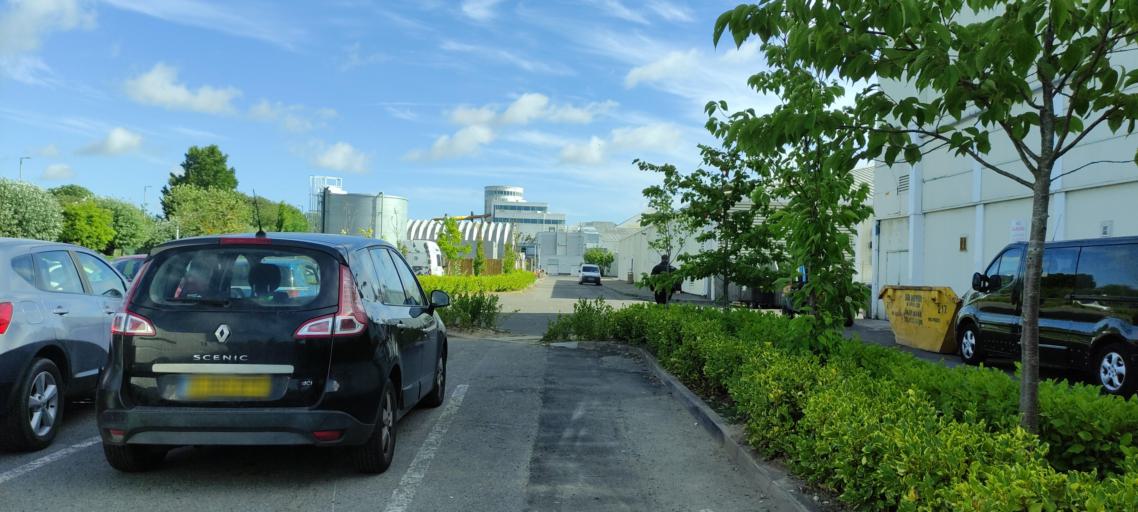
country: GB
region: England
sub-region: Lincolnshire
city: Ingoldmells
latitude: 53.1796
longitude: 0.3495
